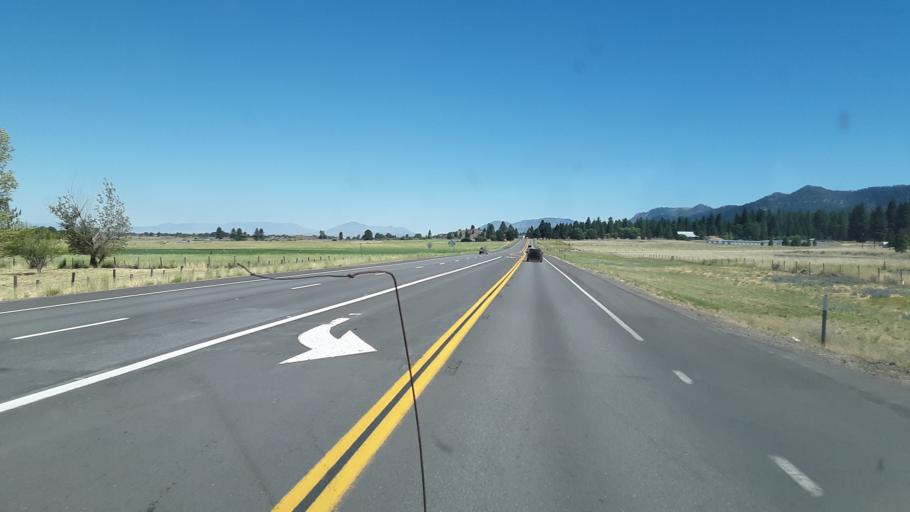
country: US
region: California
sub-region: Lassen County
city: Janesville
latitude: 40.3140
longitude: -120.5384
